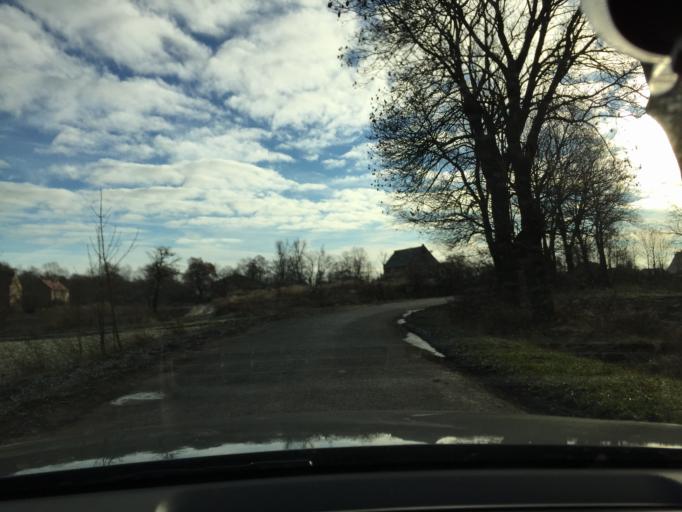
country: PL
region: Lower Silesian Voivodeship
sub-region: Powiat sredzki
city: Udanin
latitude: 51.0473
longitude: 16.5105
